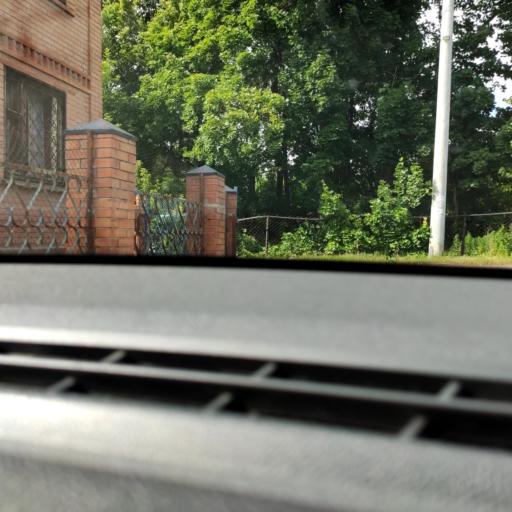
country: RU
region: Samara
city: Podstepki
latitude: 53.5845
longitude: 49.0745
